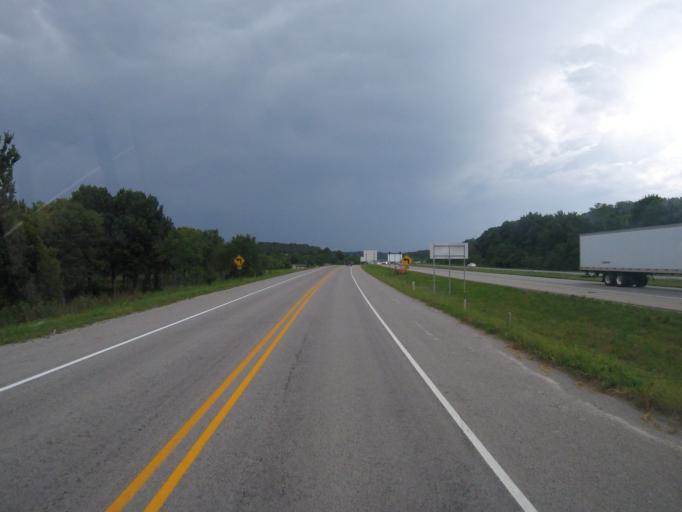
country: US
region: Arkansas
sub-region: Washington County
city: Fayetteville
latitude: 36.0477
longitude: -94.1912
